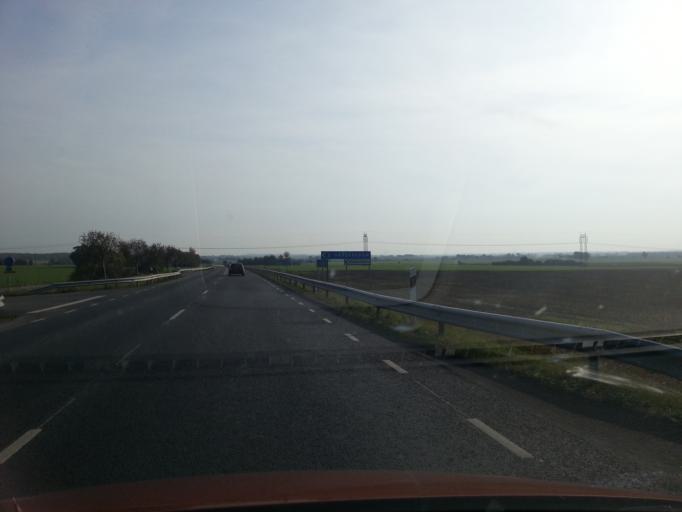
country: SE
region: Skane
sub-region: Staffanstorps Kommun
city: Staffanstorp
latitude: 55.6822
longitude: 13.2758
